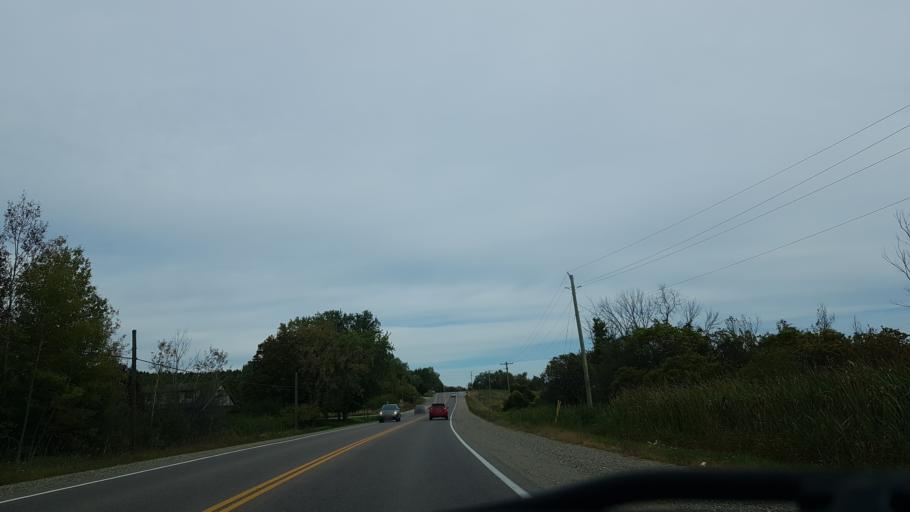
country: CA
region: Ontario
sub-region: Wellington County
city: Guelph
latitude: 43.5873
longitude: -80.2442
